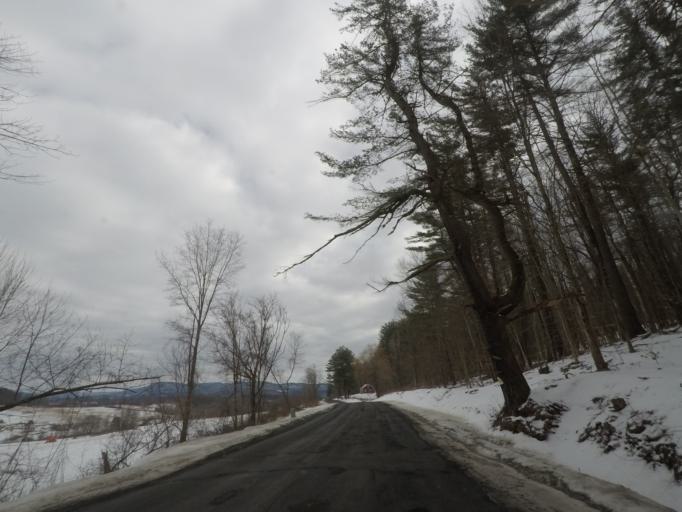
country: US
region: New York
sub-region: Rensselaer County
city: Hoosick Falls
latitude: 42.8656
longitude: -73.3685
